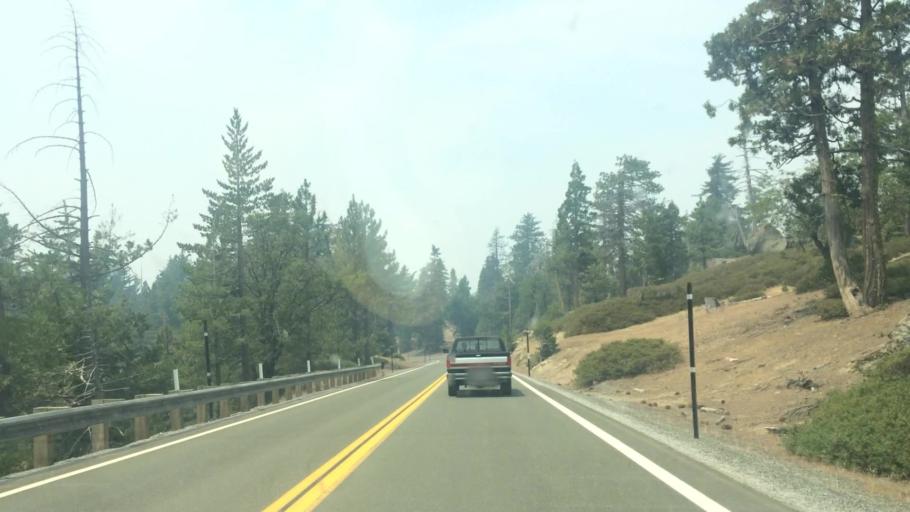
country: US
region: California
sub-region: Amador County
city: Pioneer
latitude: 38.5450
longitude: -120.3348
